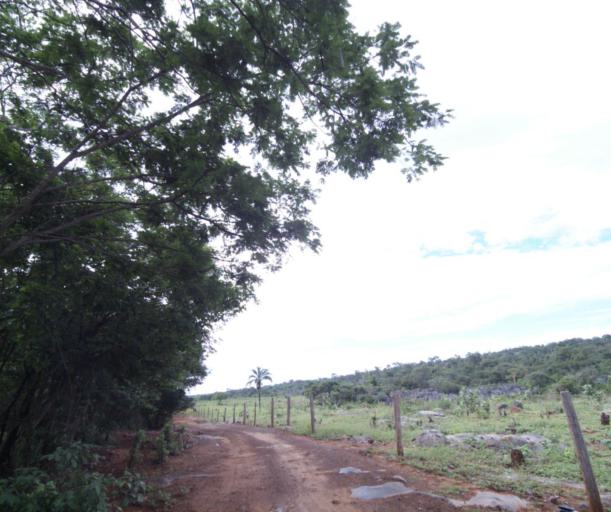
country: BR
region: Bahia
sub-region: Carinhanha
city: Carinhanha
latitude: -14.2161
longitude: -44.4452
